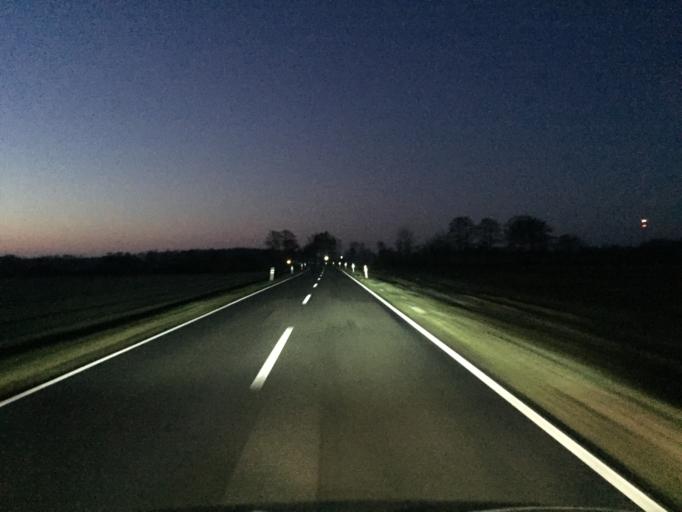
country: DE
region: Lower Saxony
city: Maasen
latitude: 52.6559
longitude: 8.8860
